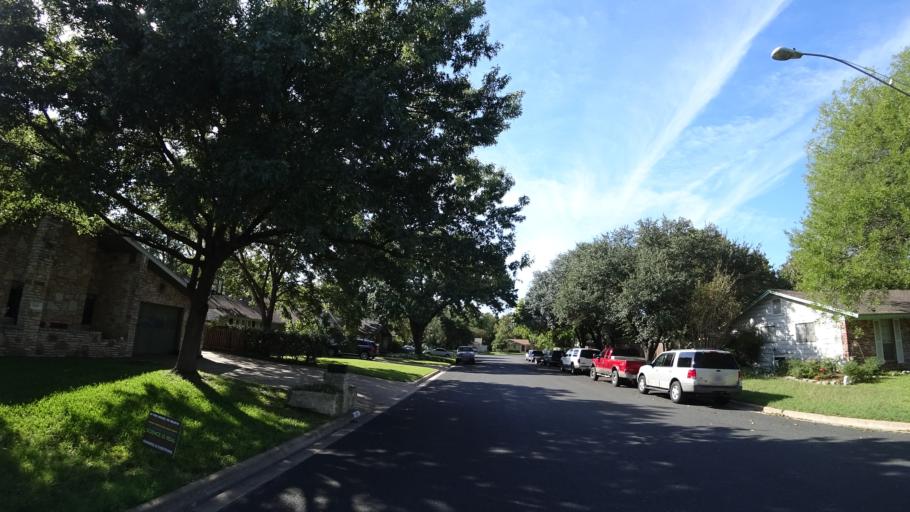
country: US
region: Texas
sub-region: Williamson County
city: Jollyville
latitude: 30.3614
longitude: -97.7361
